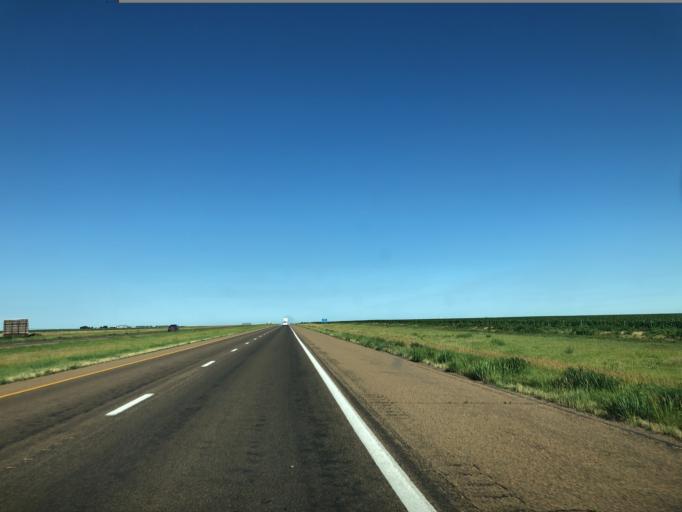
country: US
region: Kansas
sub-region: Thomas County
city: Colby
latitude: 39.3651
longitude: -101.0993
